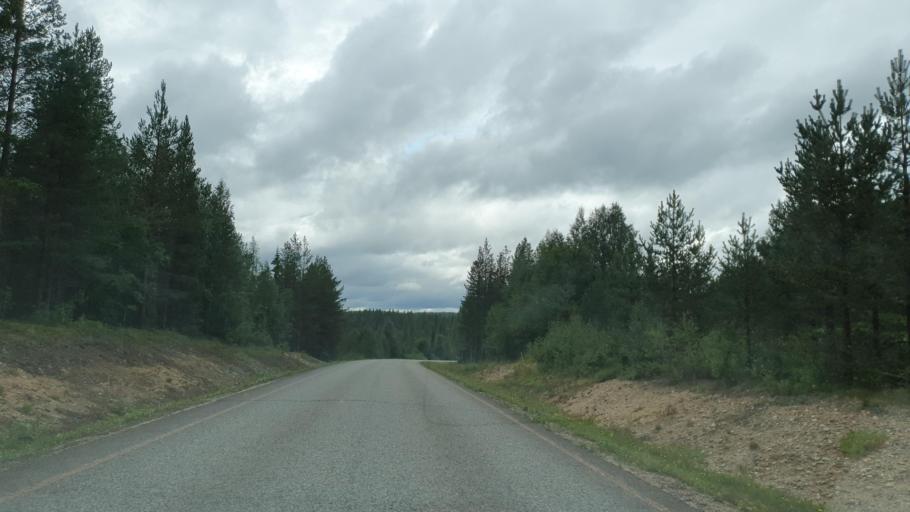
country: FI
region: Lapland
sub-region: Tunturi-Lappi
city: Kolari
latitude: 67.5076
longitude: 24.2381
